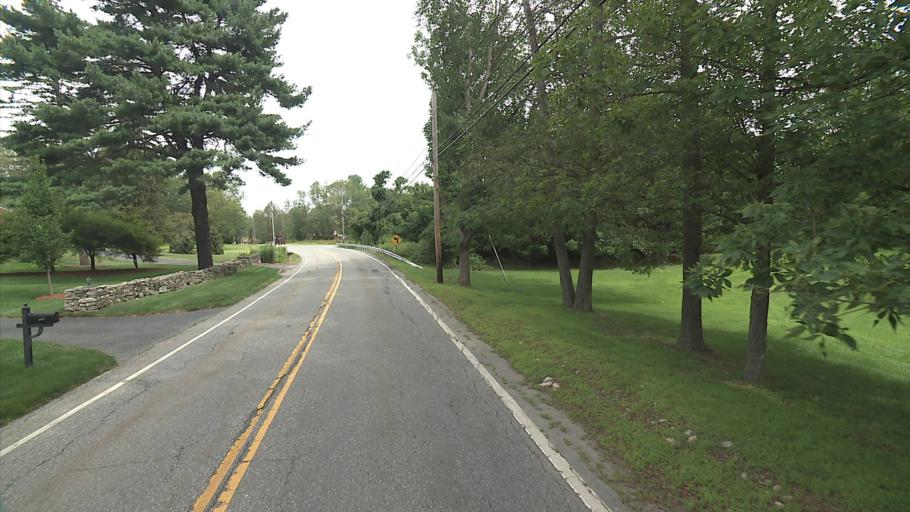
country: US
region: Massachusetts
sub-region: Worcester County
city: Webster
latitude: 42.0201
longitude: -71.8441
